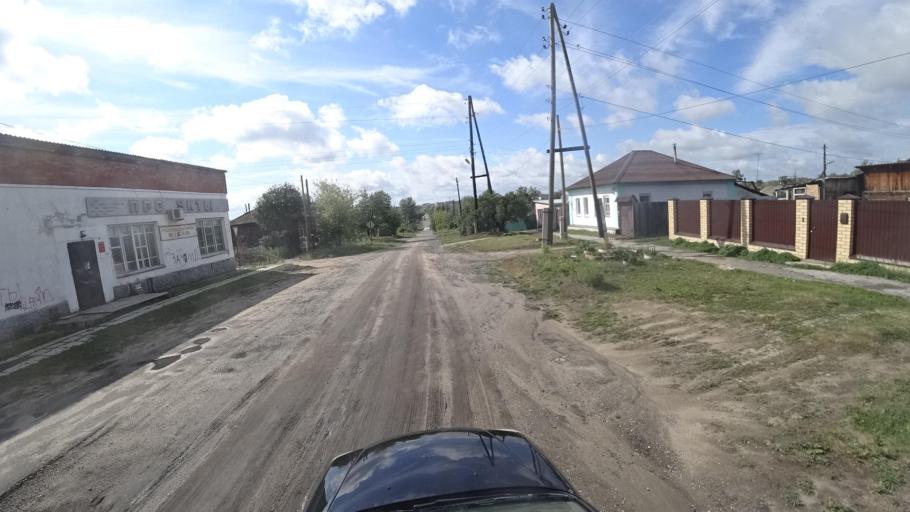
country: RU
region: Sverdlovsk
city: Kamyshlov
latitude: 56.8393
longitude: 62.7233
